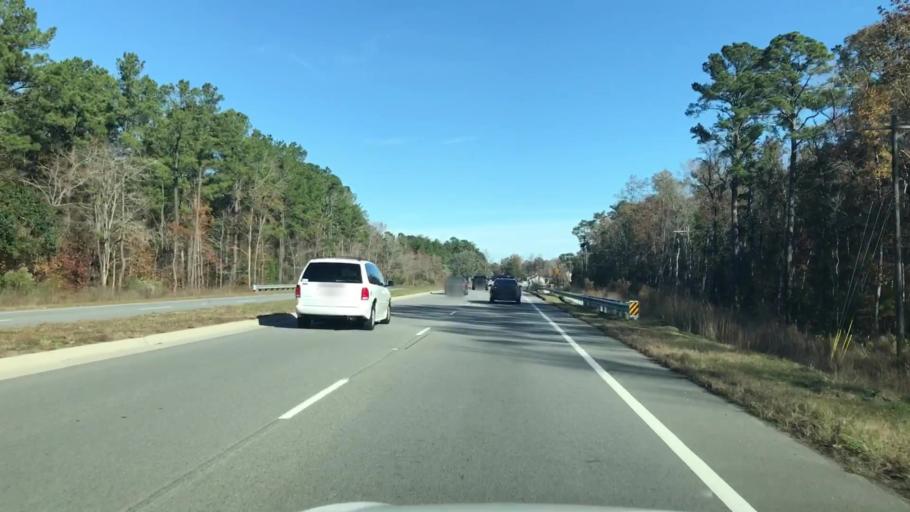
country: US
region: South Carolina
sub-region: Dorchester County
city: Centerville
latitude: 32.9542
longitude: -80.2016
